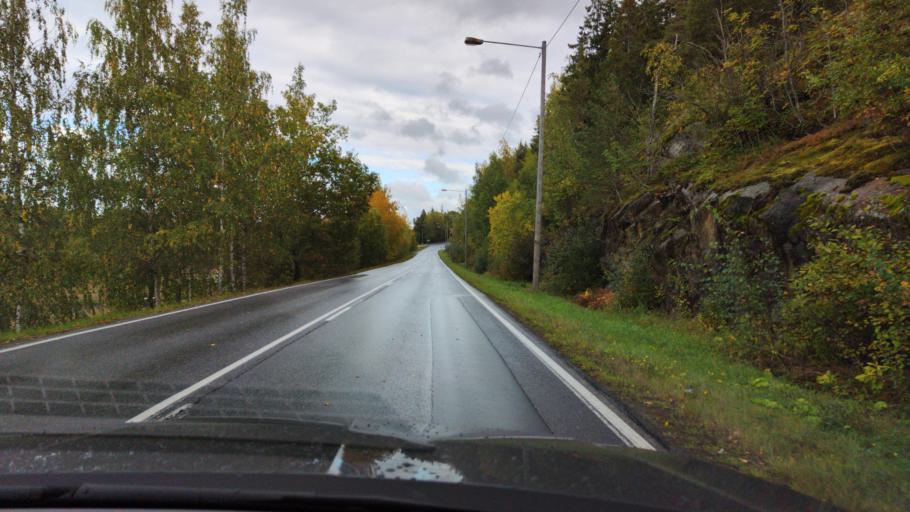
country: FI
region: Varsinais-Suomi
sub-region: Turku
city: Turku
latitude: 60.3660
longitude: 22.2057
